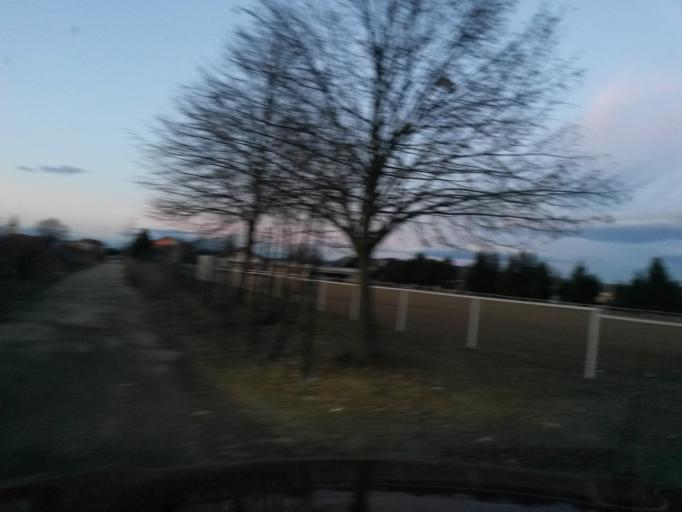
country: SK
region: Kosicky
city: Kosice
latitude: 48.7044
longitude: 21.3292
